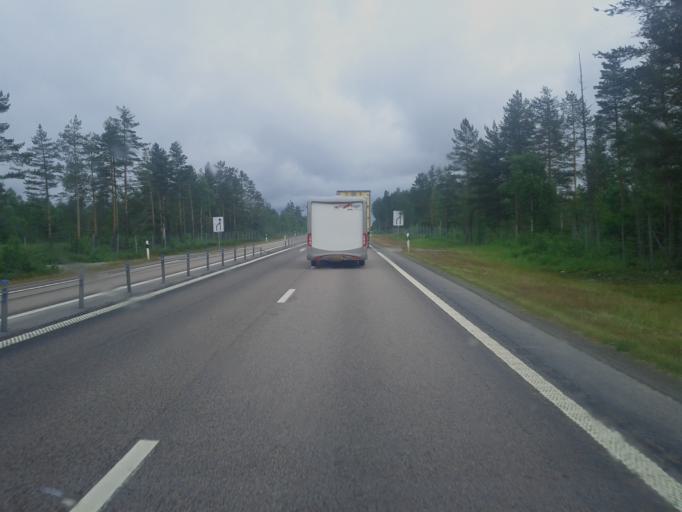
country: SE
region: Vaesternorrland
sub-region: Haernoesands Kommun
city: Haernoesand
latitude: 62.5660
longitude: 17.7338
